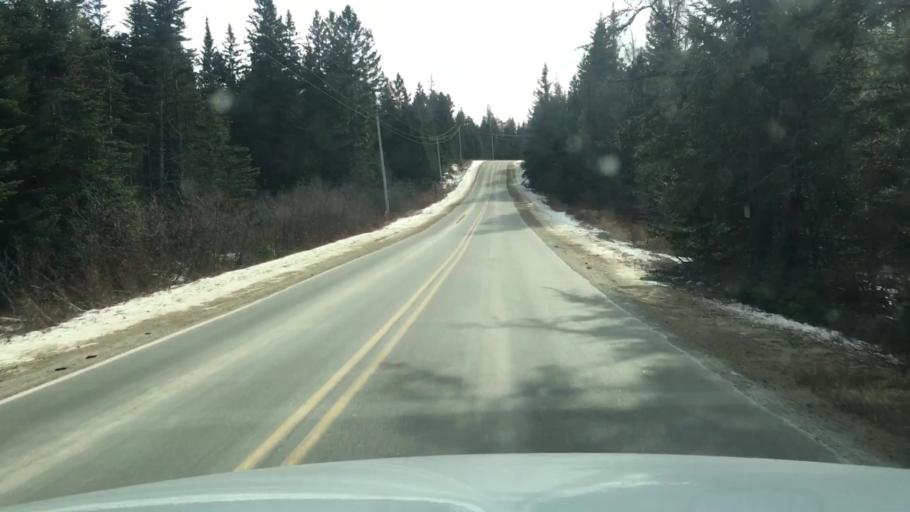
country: US
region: Maine
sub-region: Washington County
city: Jonesport
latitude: 44.6358
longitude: -67.5932
